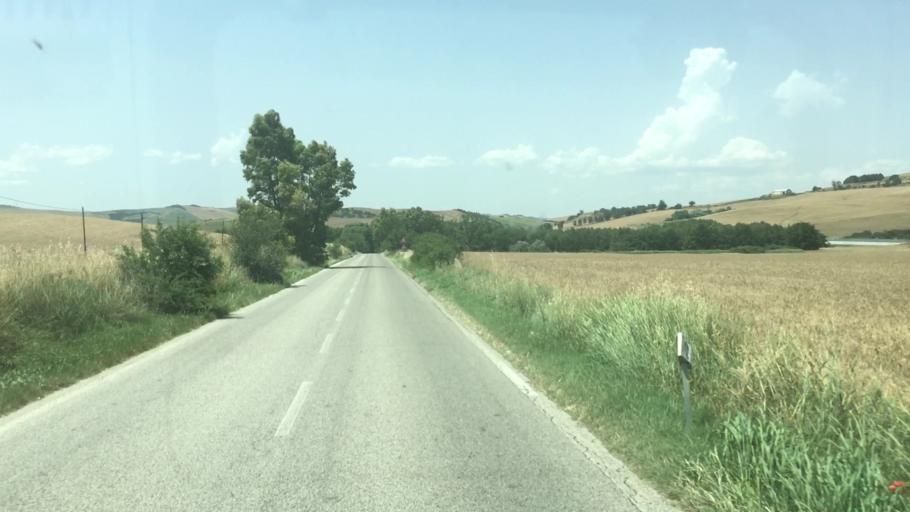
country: IT
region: Basilicate
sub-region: Provincia di Matera
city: La Martella
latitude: 40.6692
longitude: 16.4846
